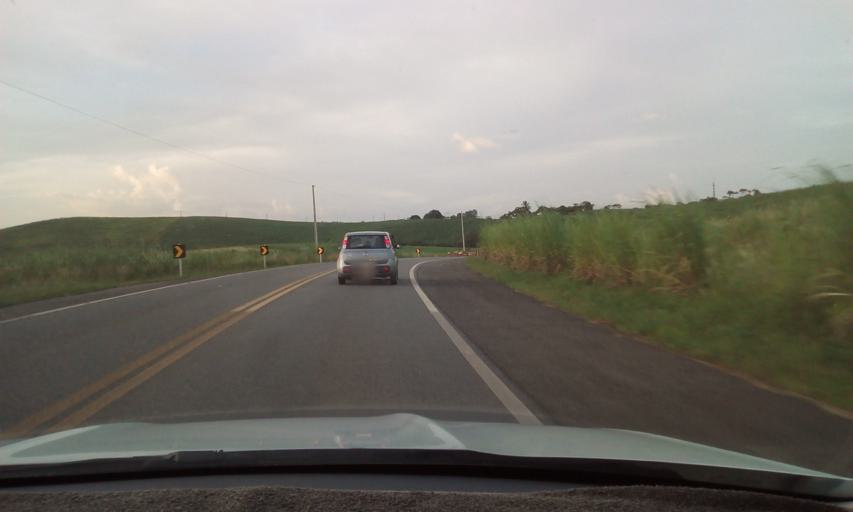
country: BR
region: Pernambuco
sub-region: Vicencia
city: Vicencia
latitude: -7.6205
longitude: -35.2415
